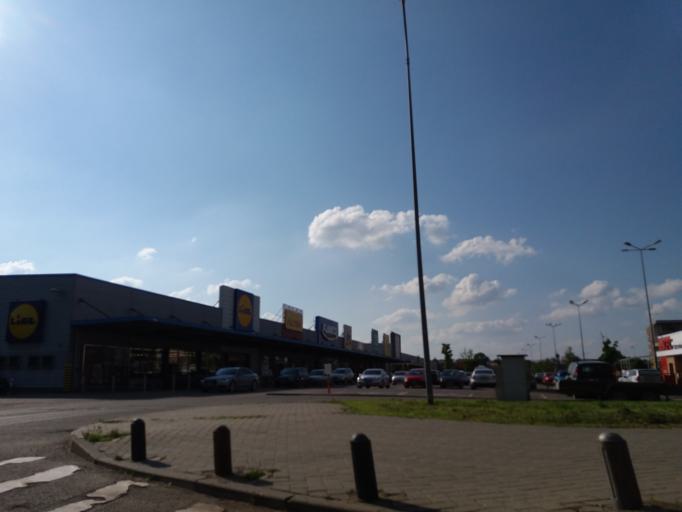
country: RO
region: Arad
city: Arad
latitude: 46.1848
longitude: 21.3154
